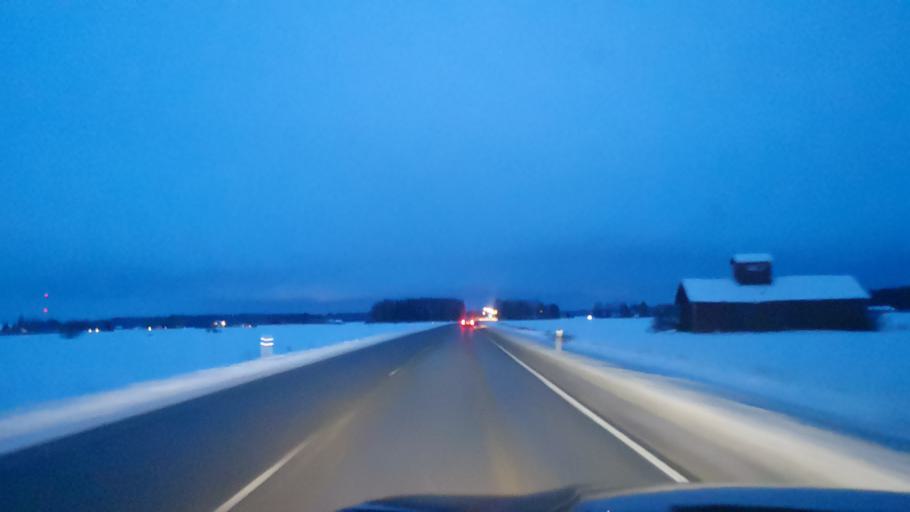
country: FI
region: Varsinais-Suomi
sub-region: Loimaa
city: Loimaa
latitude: 60.8792
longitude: 23.0761
